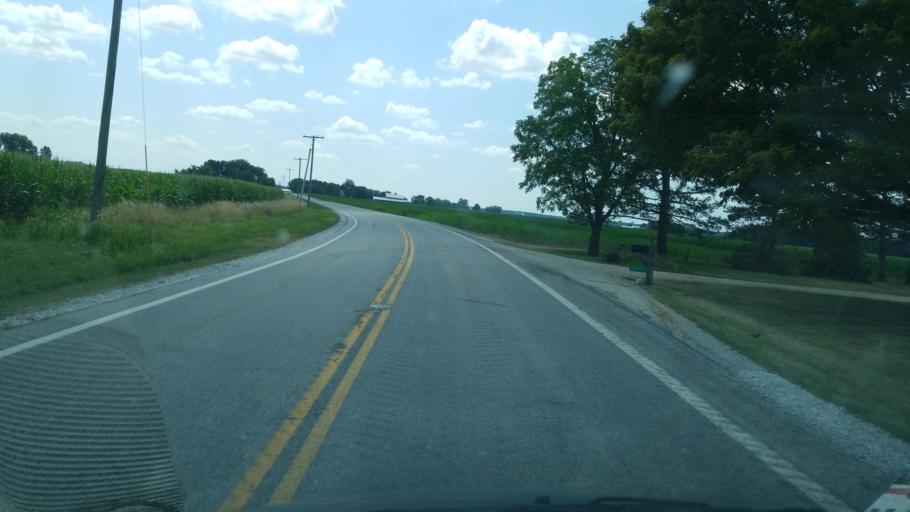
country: US
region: Ohio
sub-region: Champaign County
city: North Lewisburg
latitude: 40.1500
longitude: -83.5071
